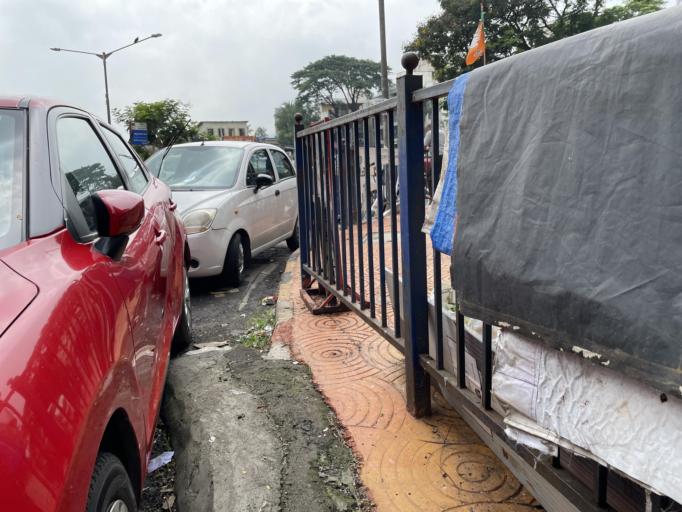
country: IN
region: Maharashtra
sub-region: Mumbai Suburban
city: Borivli
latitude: 19.2568
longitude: 72.8556
